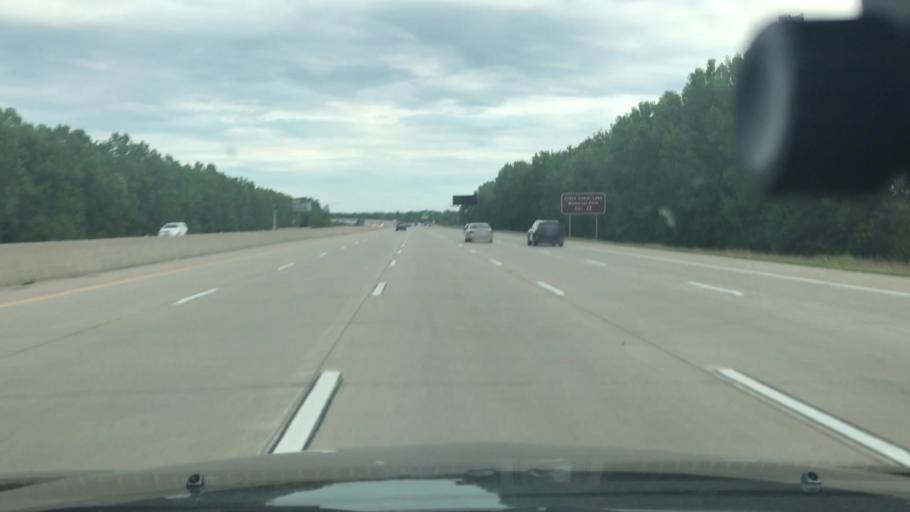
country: US
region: Missouri
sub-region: Saint Charles County
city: Saint Charles
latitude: 38.7171
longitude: -90.5096
